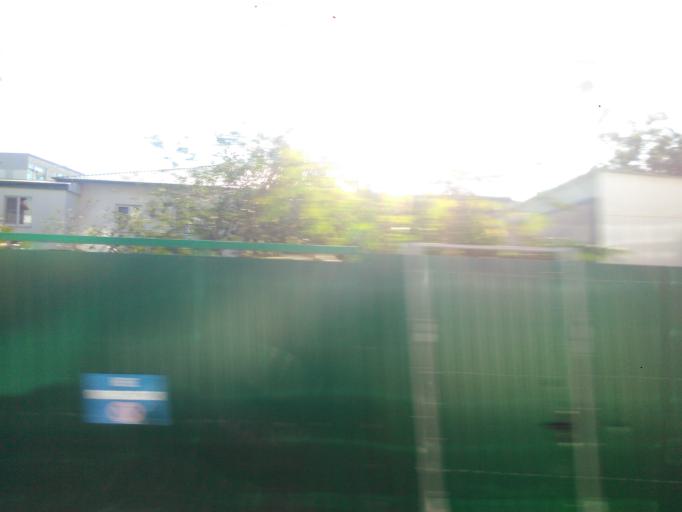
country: RU
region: Krasnodarskiy
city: Gelendzhik
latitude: 44.5508
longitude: 38.0620
